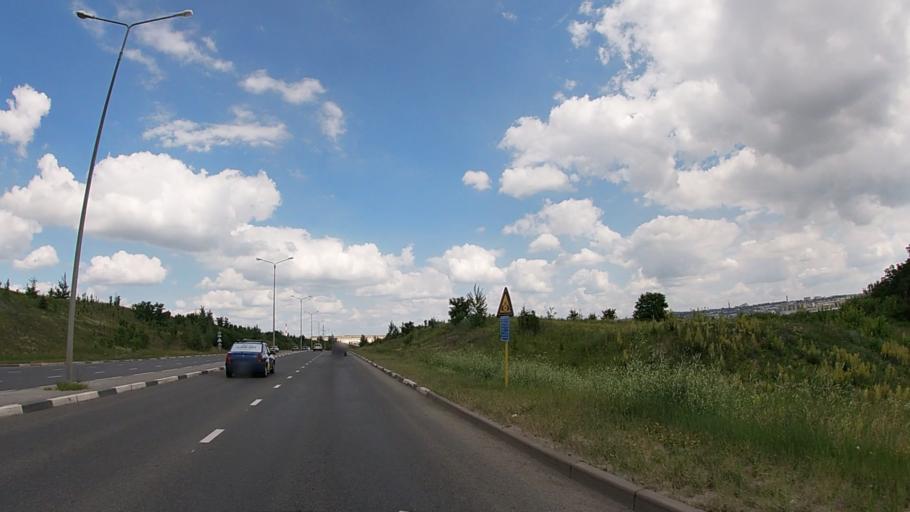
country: RU
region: Belgorod
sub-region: Belgorodskiy Rayon
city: Belgorod
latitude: 50.6010
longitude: 36.5300
